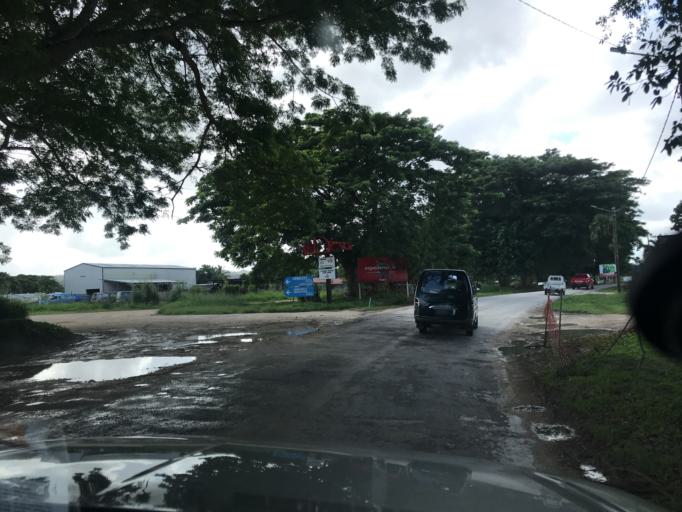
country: VU
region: Shefa
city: Port-Vila
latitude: -17.7057
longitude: 168.3157
